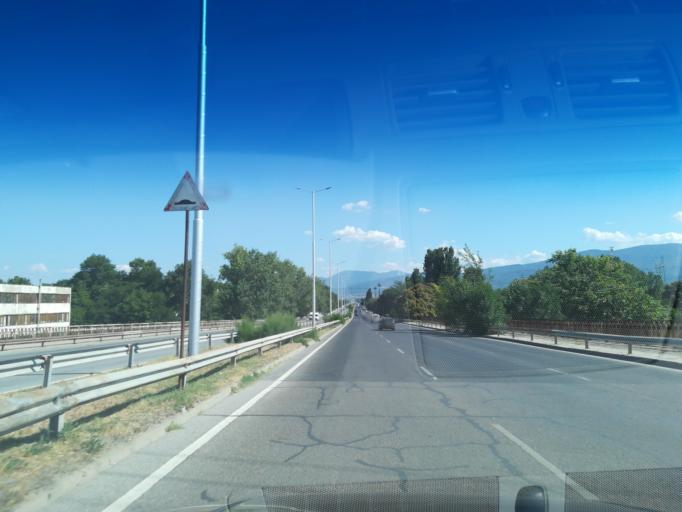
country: BG
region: Plovdiv
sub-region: Obshtina Plovdiv
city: Plovdiv
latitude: 42.1152
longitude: 24.7777
